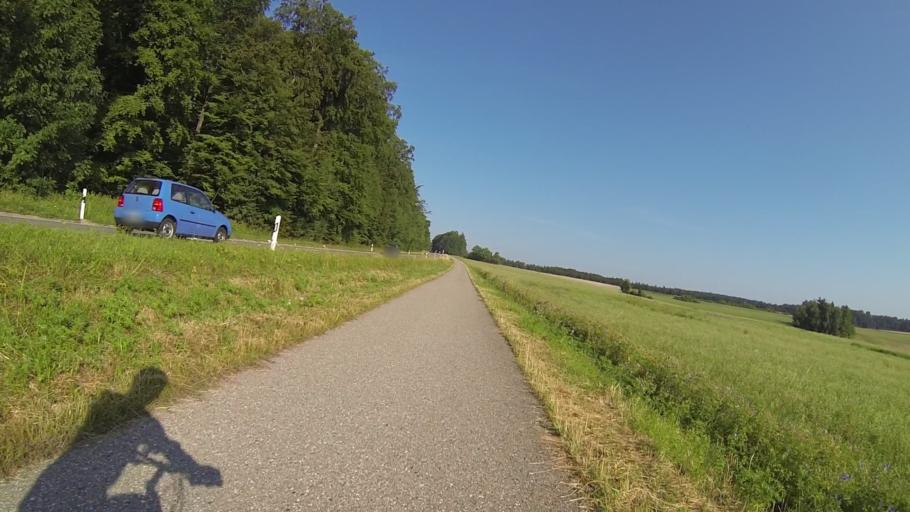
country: DE
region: Baden-Wuerttemberg
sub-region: Regierungsbezirk Stuttgart
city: Heidenheim an der Brenz
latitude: 48.6986
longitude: 10.1286
